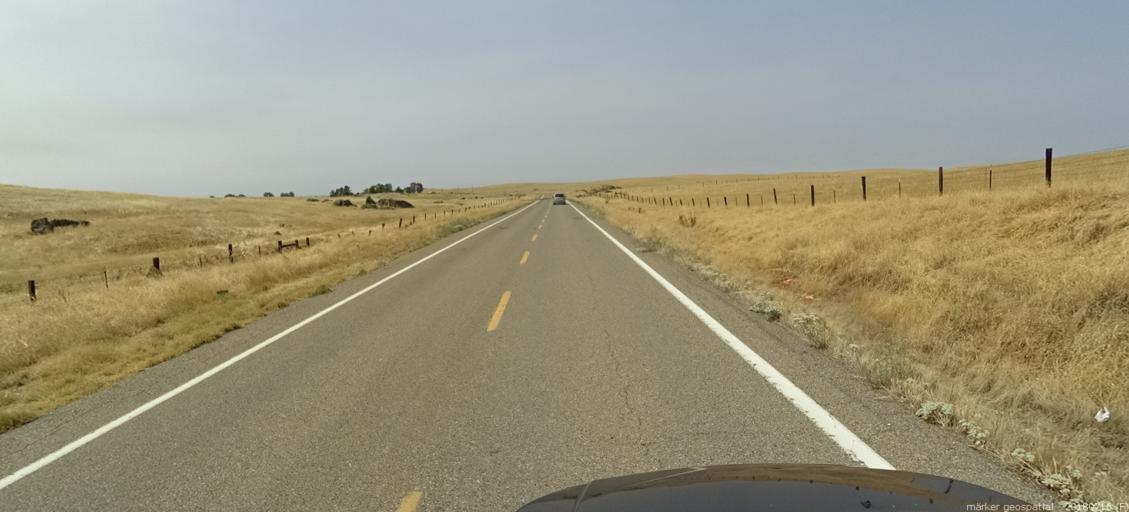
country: US
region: California
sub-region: Madera County
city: Bonadelle Ranchos-Madera Ranchos
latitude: 37.1132
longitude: -119.9379
